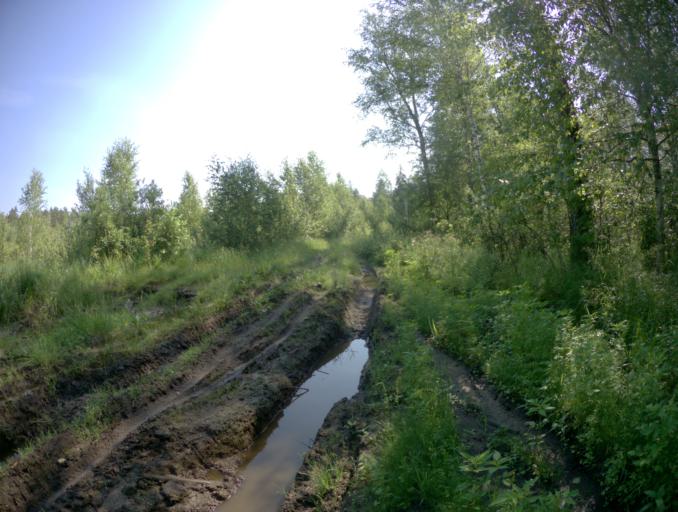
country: RU
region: Vladimir
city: Vyazniki
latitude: 56.3426
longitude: 42.1674
